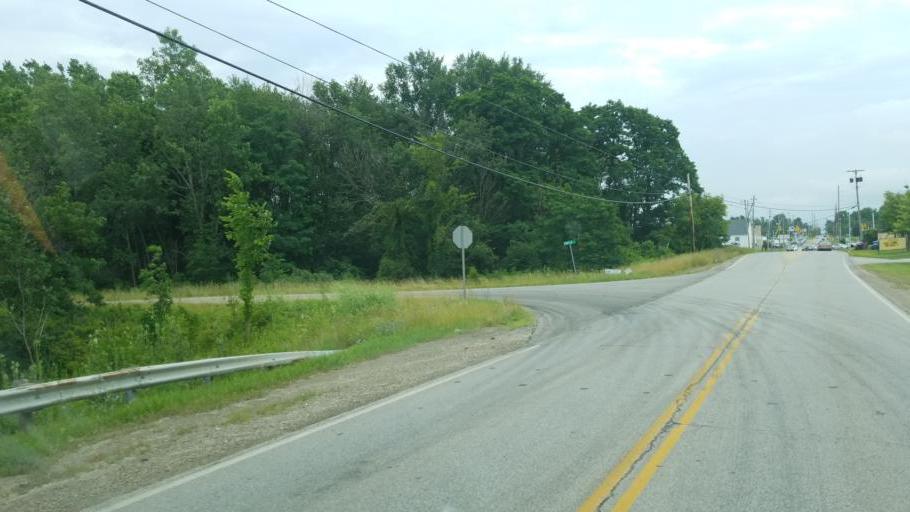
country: US
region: Ohio
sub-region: Richland County
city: Ontario
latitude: 40.7710
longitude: -82.5709
